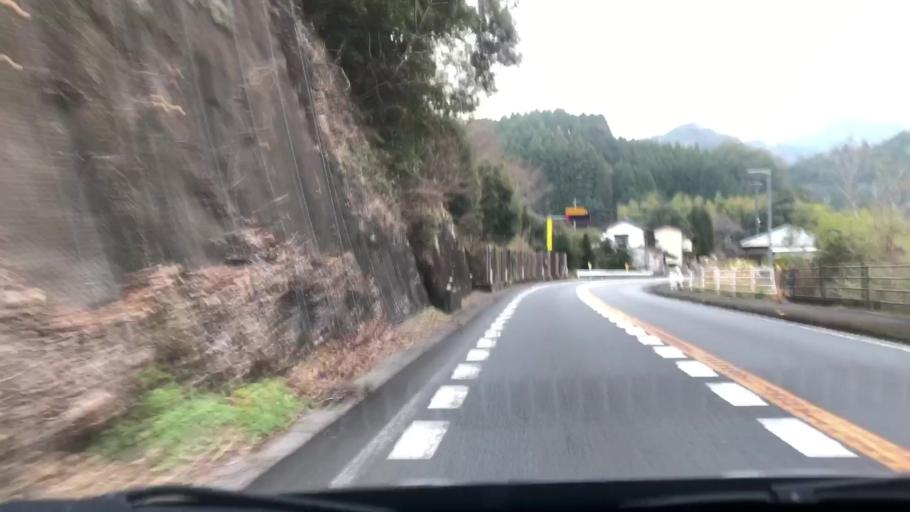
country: JP
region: Oita
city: Usuki
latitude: 32.9968
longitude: 131.7571
